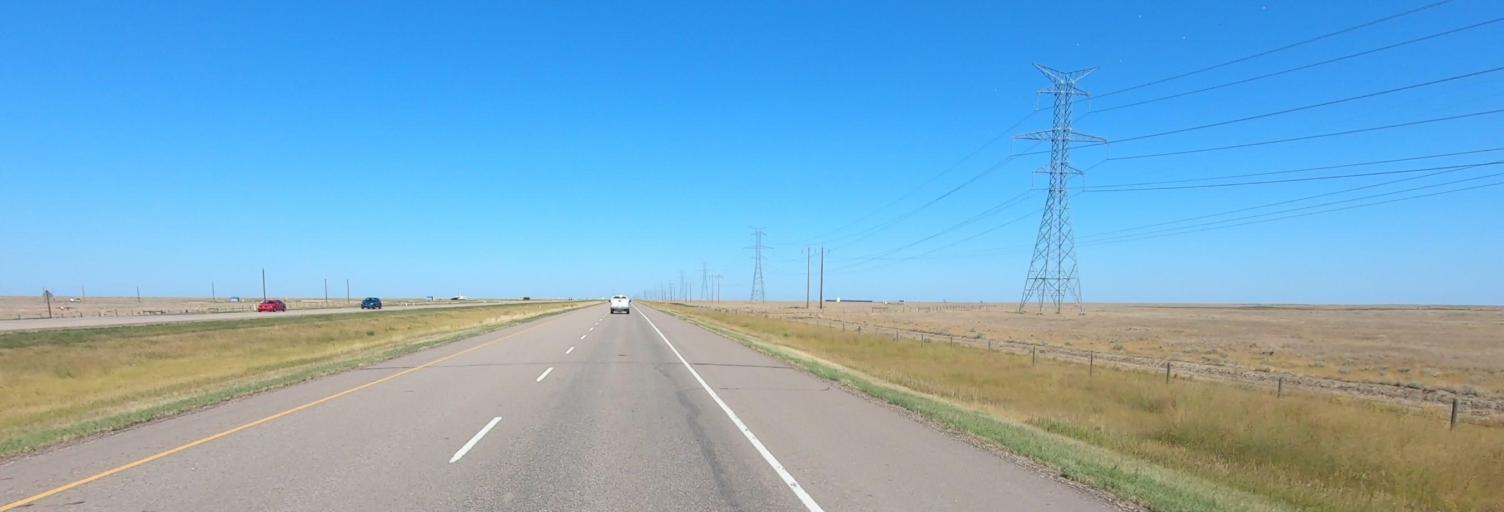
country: CA
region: Alberta
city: Brooks
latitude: 50.3964
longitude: -111.4806
